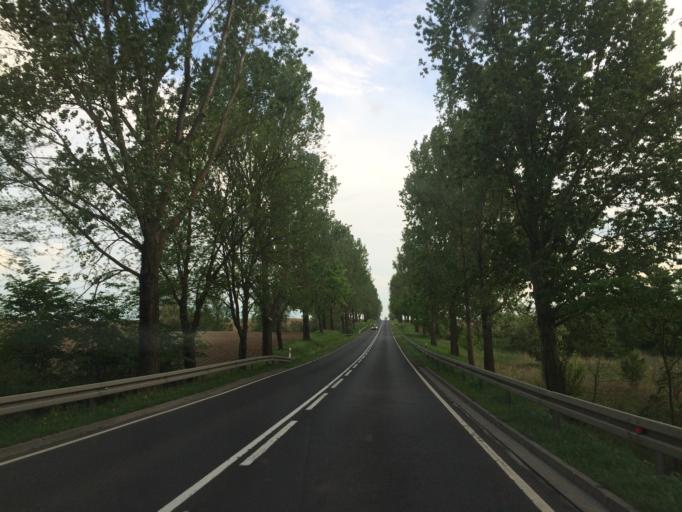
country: PL
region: Kujawsko-Pomorskie
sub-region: Powiat brodnicki
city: Brzozie
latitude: 53.3535
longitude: 19.5696
